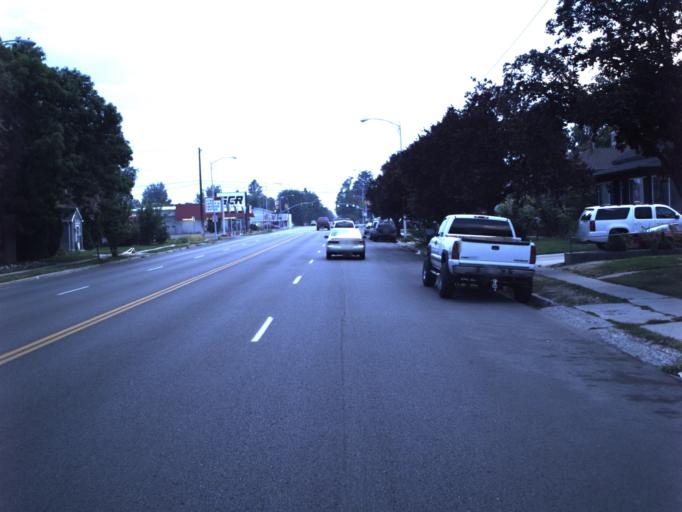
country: US
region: Utah
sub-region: Utah County
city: Provo
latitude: 40.2298
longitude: -111.6642
